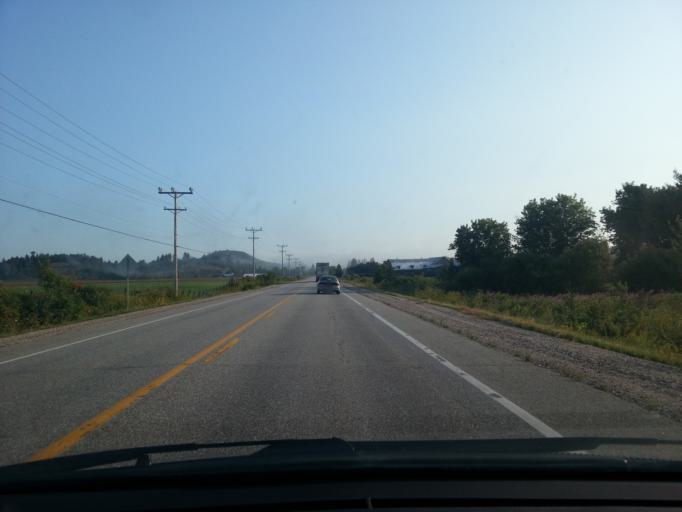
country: CA
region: Quebec
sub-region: Outaouais
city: Wakefield
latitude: 45.9761
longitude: -76.0231
